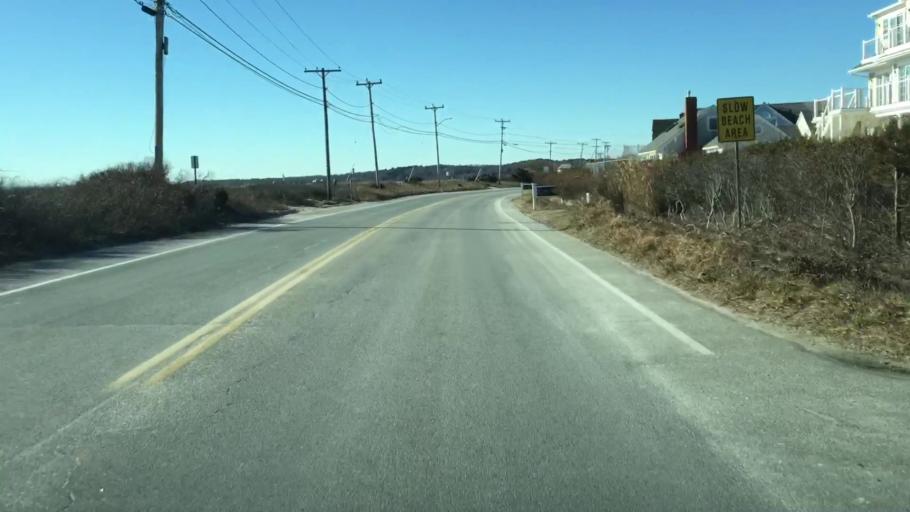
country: US
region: Massachusetts
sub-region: Barnstable County
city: Falmouth
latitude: 41.5422
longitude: -70.6197
